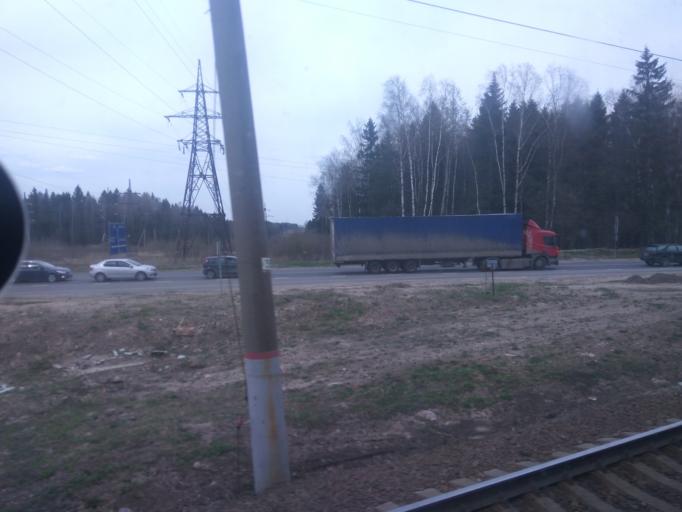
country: RU
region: Moskovskaya
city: Skoropuskovskiy
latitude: 56.3632
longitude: 38.1950
